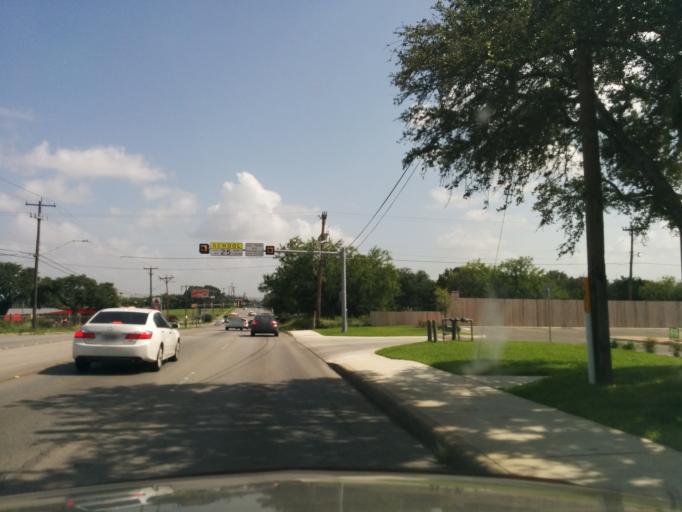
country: US
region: Texas
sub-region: Bexar County
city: Leon Valley
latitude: 29.5506
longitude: -98.6149
